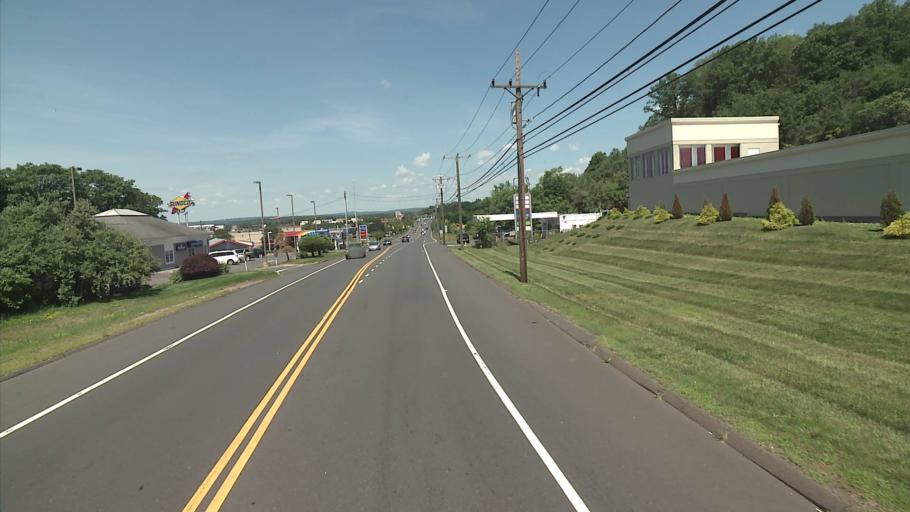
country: US
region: Connecticut
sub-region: Hartford County
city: Plainville
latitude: 41.6722
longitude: -72.8353
